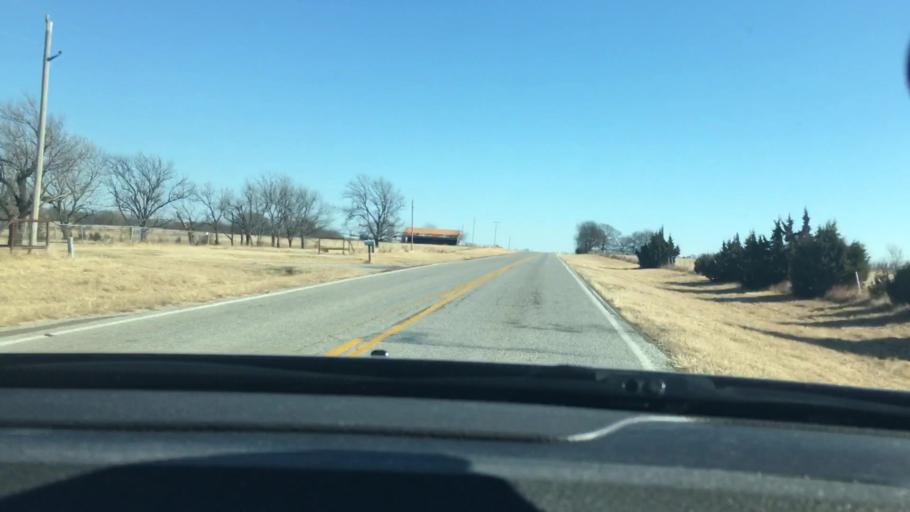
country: US
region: Oklahoma
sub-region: Garvin County
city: Wynnewood
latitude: 34.6515
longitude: -97.0958
